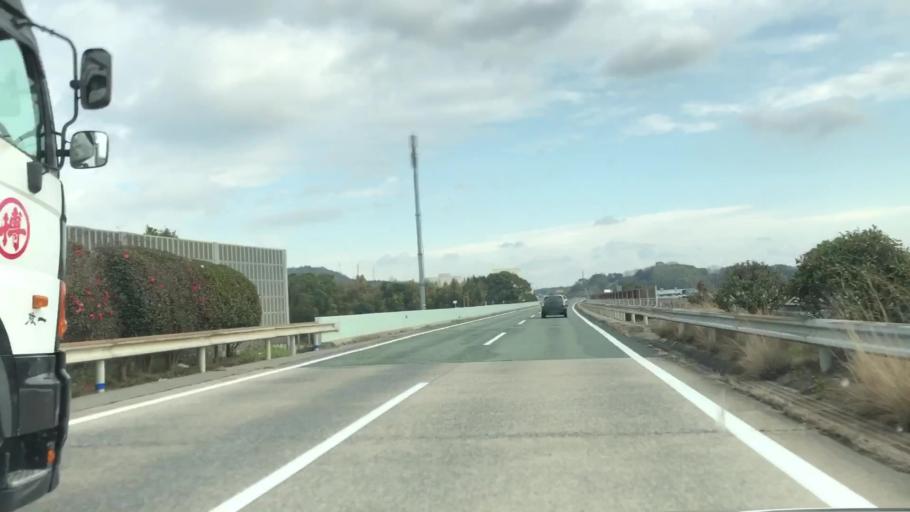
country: JP
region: Saga Prefecture
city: Kanzakimachi-kanzaki
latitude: 33.3543
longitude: 130.4016
